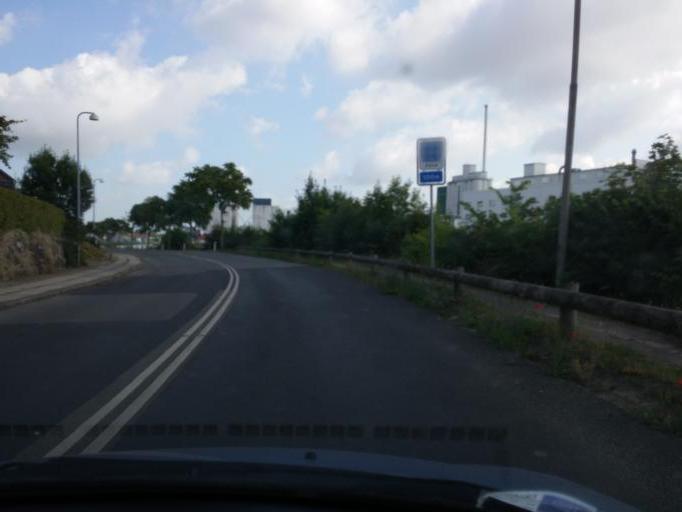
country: DK
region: South Denmark
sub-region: Odense Kommune
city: Odense
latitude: 55.4123
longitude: 10.3792
